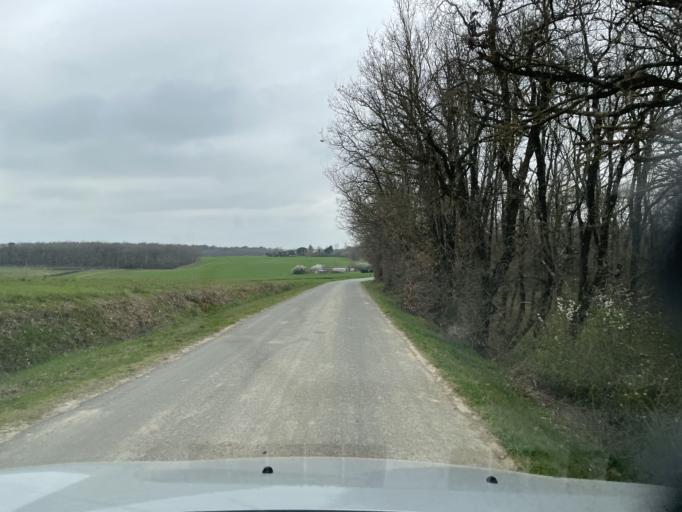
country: FR
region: Midi-Pyrenees
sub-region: Departement du Gers
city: Pujaudran
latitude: 43.6127
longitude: 1.1668
